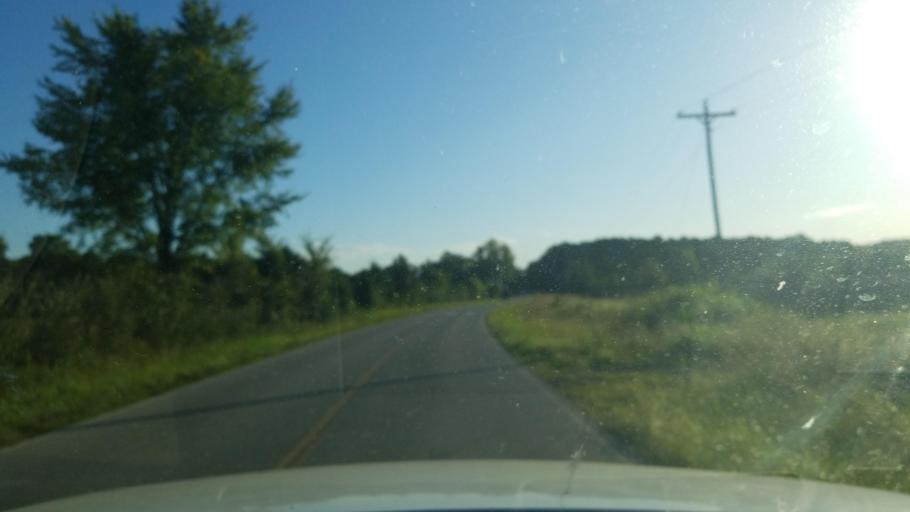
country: US
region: Illinois
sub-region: Hardin County
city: Rosiclare
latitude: 37.5694
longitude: -88.4010
